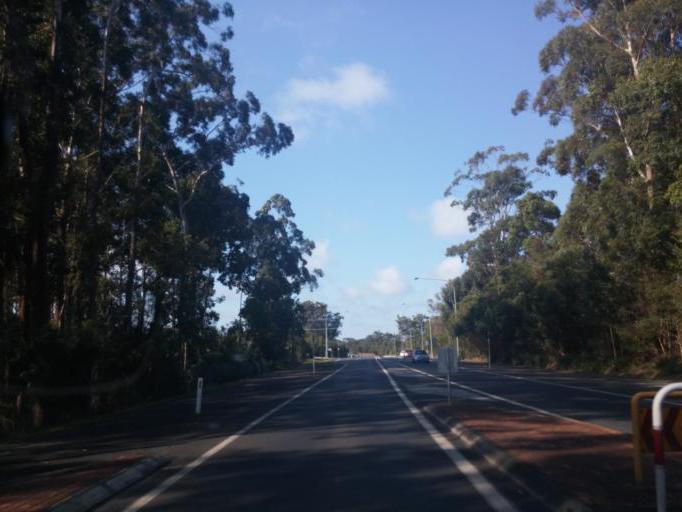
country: AU
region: New South Wales
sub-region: Coffs Harbour
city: Coffs Harbour
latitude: -30.2964
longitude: 153.1292
